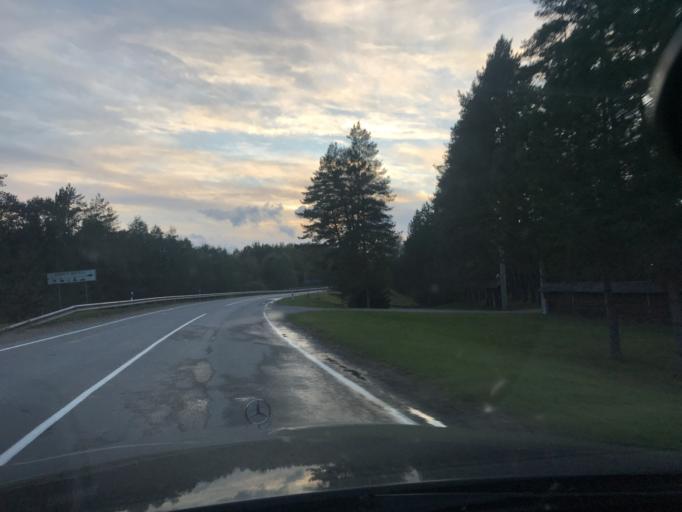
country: EE
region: Valgamaa
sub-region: Torva linn
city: Torva
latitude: 57.9861
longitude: 26.0517
